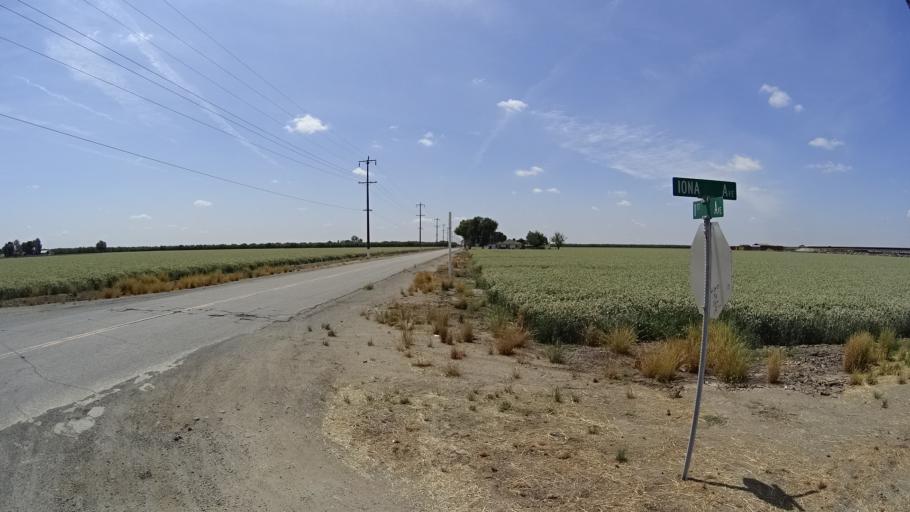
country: US
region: California
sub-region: Tulare County
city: Goshen
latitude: 36.2834
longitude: -119.4745
